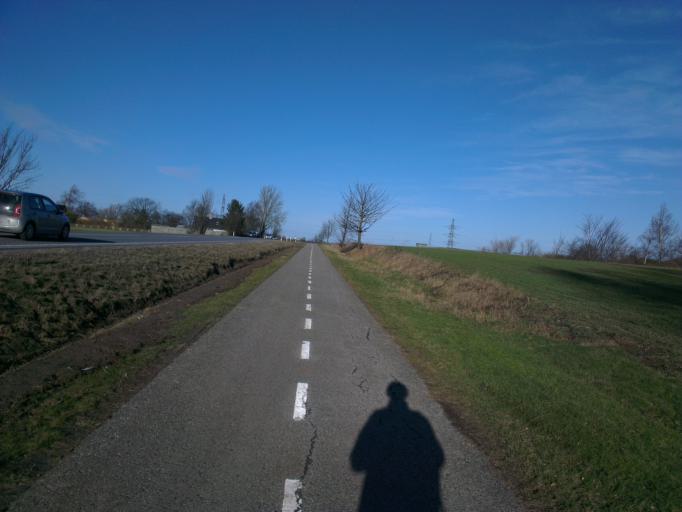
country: DK
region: Capital Region
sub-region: Frederikssund Kommune
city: Skibby
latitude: 55.7962
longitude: 11.9796
